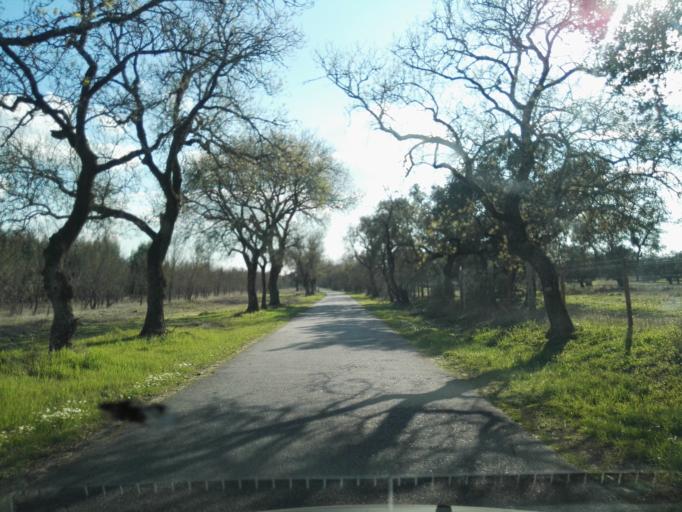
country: PT
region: Evora
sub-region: Evora
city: Evora
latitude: 38.5454
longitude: -7.9361
